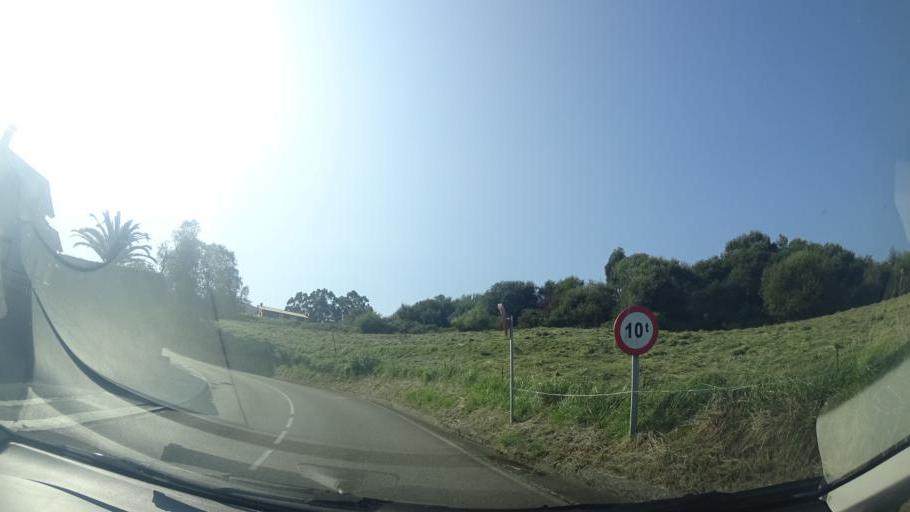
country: ES
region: Asturias
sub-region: Province of Asturias
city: Colunga
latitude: 43.4683
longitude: -5.1896
